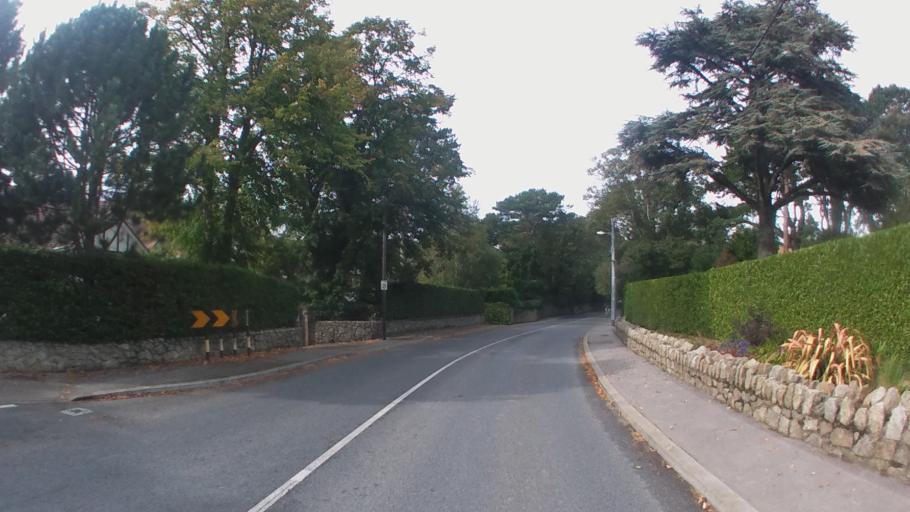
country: IE
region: Leinster
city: Foxrock
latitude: 53.2592
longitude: -6.1766
